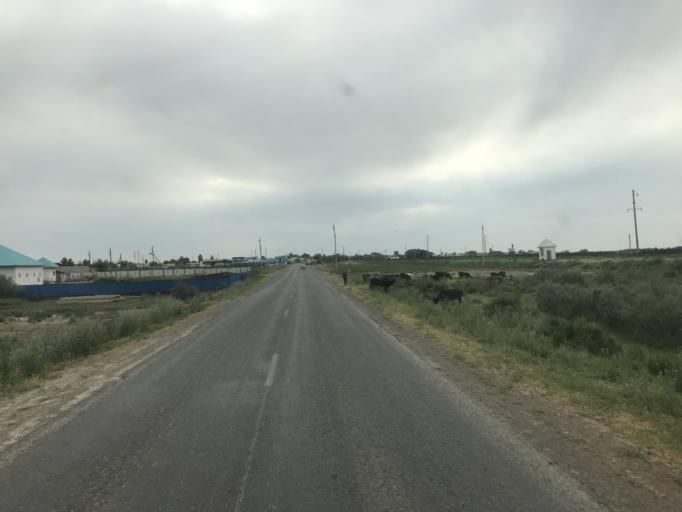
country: KZ
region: Ongtustik Qazaqstan
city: Asykata
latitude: 40.9080
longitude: 68.3753
